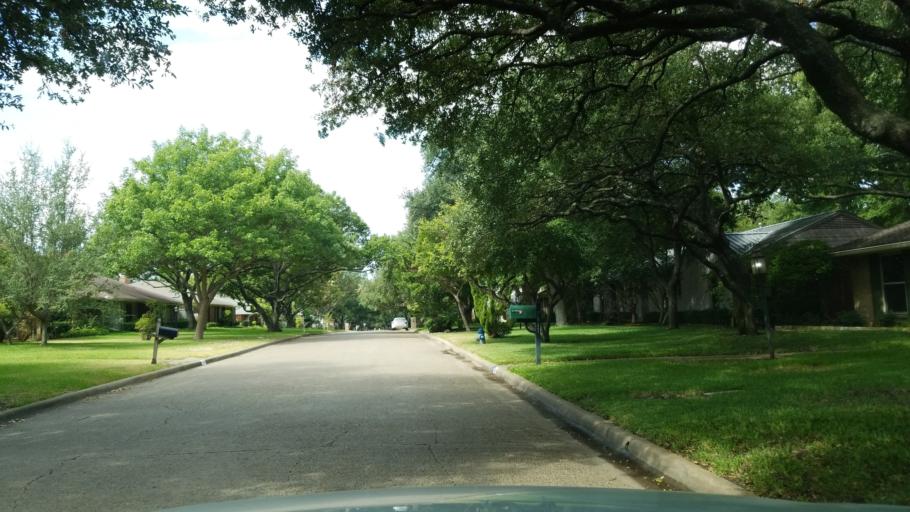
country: US
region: Texas
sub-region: Dallas County
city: Richardson
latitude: 32.9531
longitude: -96.7728
